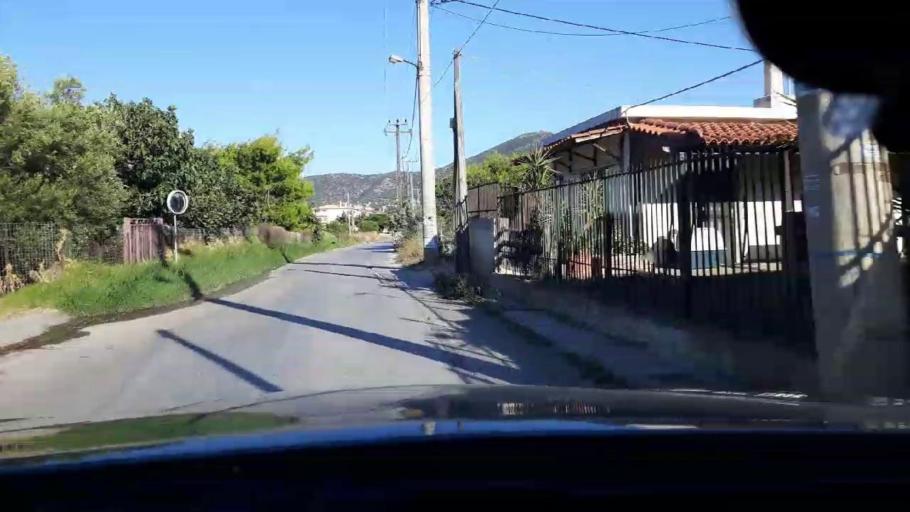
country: GR
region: Attica
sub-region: Nomarchia Anatolikis Attikis
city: Limin Mesoyaias
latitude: 37.8691
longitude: 24.0179
